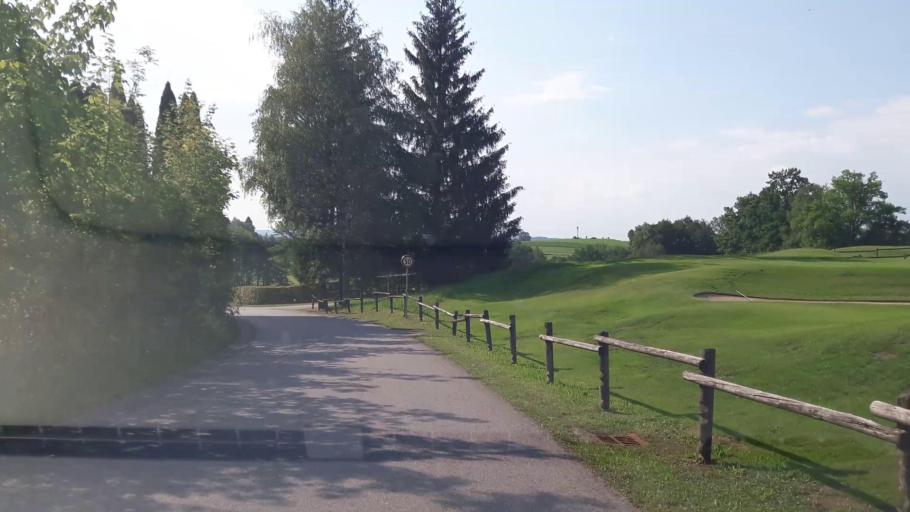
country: AT
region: Salzburg
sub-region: Politischer Bezirk Salzburg-Umgebung
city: Henndorf am Wallersee
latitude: 47.8917
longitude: 13.2059
